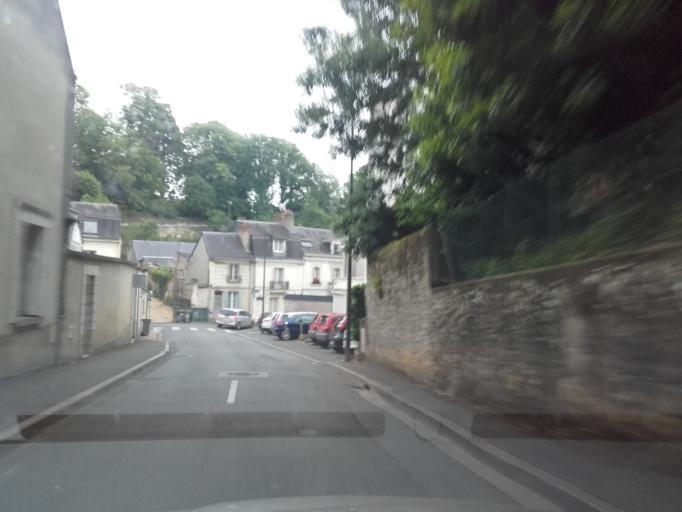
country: FR
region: Centre
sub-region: Departement d'Indre-et-Loire
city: Tours
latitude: 47.4046
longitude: 0.6944
